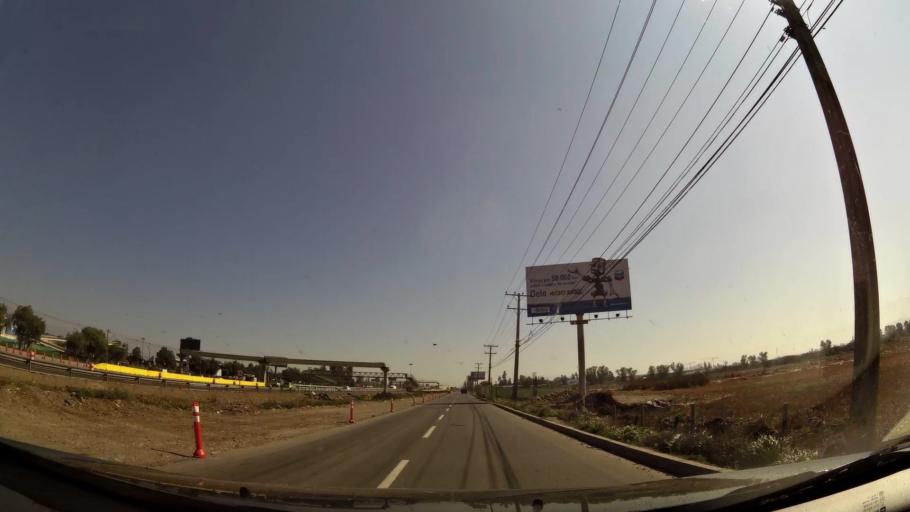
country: CL
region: Santiago Metropolitan
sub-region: Provincia de Chacabuco
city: Chicureo Abajo
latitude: -33.3210
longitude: -70.7200
